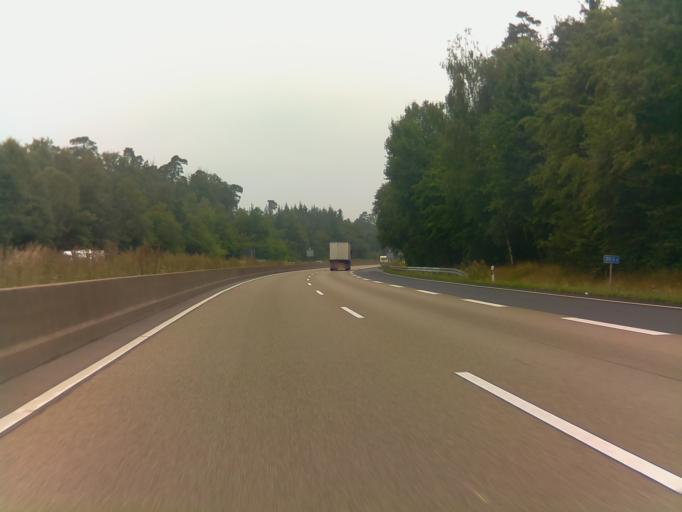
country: DE
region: Hesse
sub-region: Regierungsbezirk Kassel
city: Petersberg
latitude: 50.6260
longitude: 9.6764
